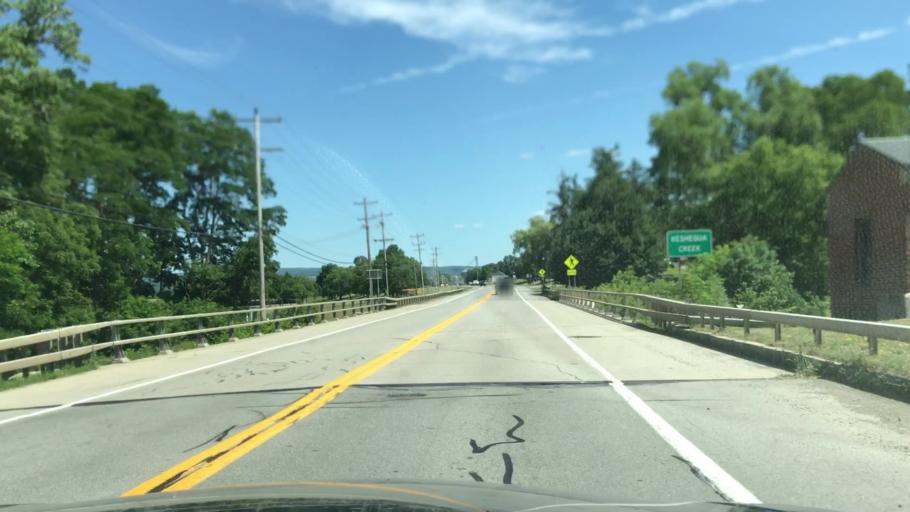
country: US
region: New York
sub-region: Livingston County
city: Mount Morris
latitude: 42.6835
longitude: -77.8289
